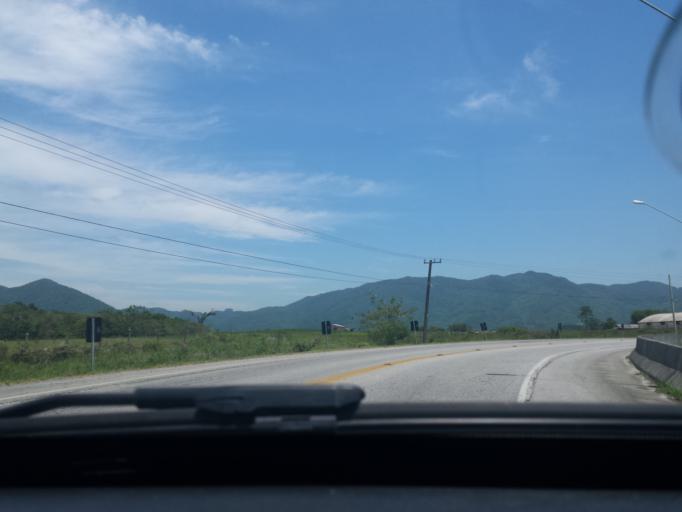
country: BR
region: Santa Catarina
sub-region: Porto Belo
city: Porto Belo
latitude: -27.1644
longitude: -48.6126
